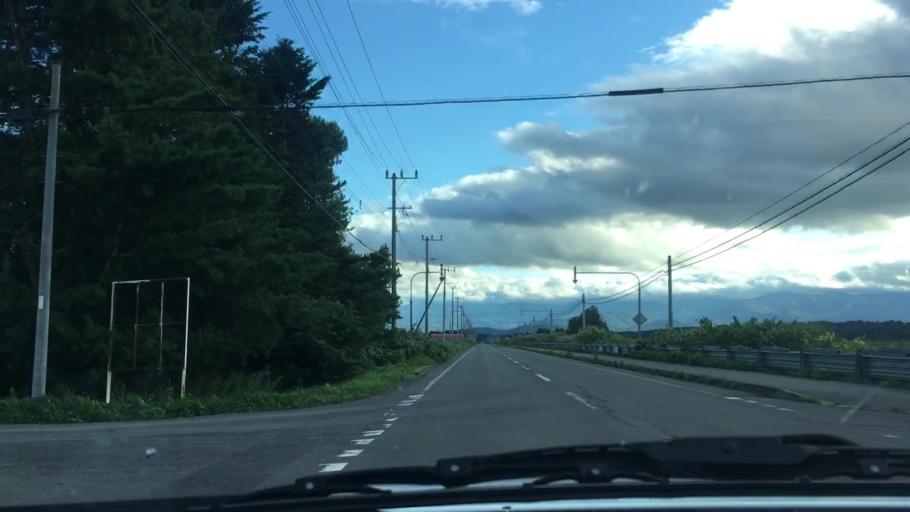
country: JP
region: Hokkaido
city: Otofuke
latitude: 43.1536
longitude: 142.9013
